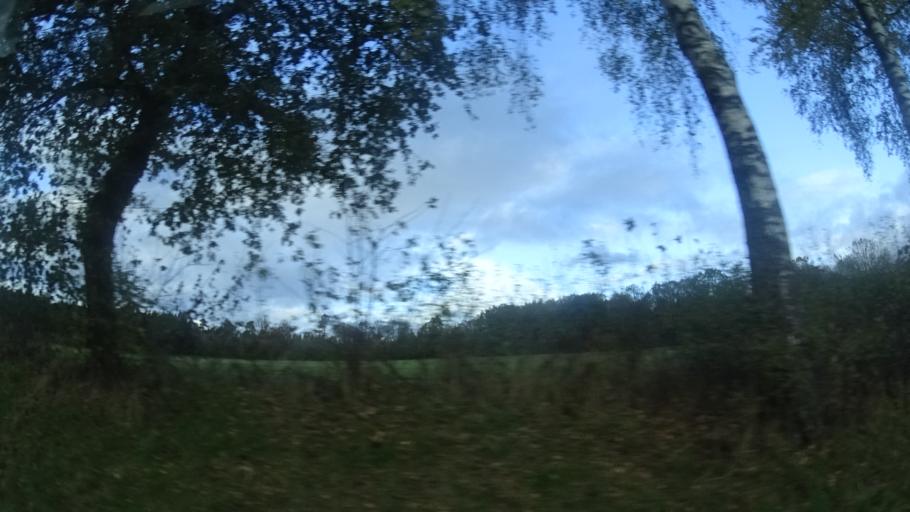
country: DE
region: Hesse
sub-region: Regierungsbezirk Kassel
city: Flieden
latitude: 50.4554
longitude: 9.5538
